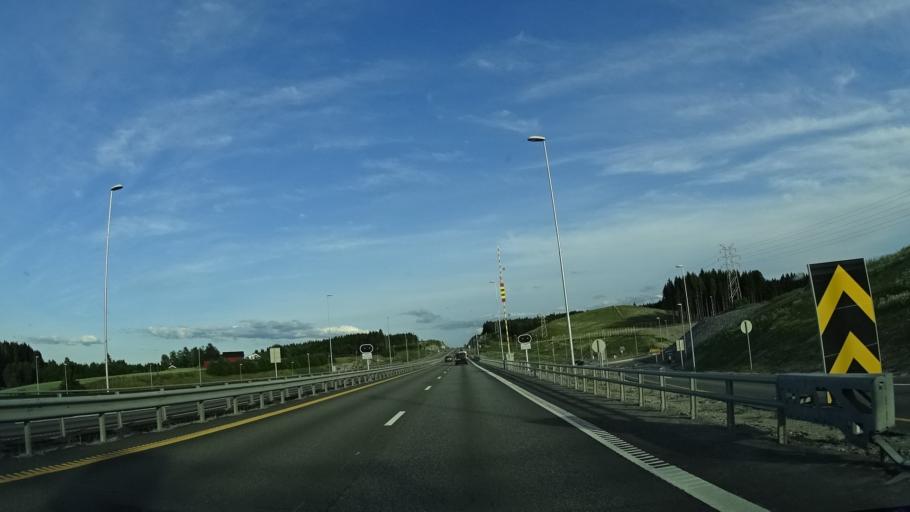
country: NO
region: Ostfold
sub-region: Hobol
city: Knappstad
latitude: 59.6197
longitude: 11.0032
